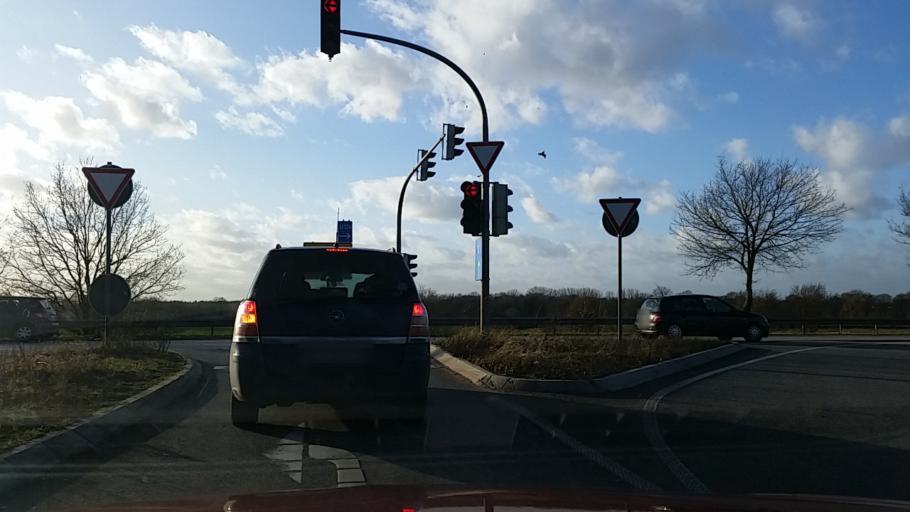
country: DE
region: Schleswig-Holstein
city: Glinde
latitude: 53.5610
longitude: 10.2281
